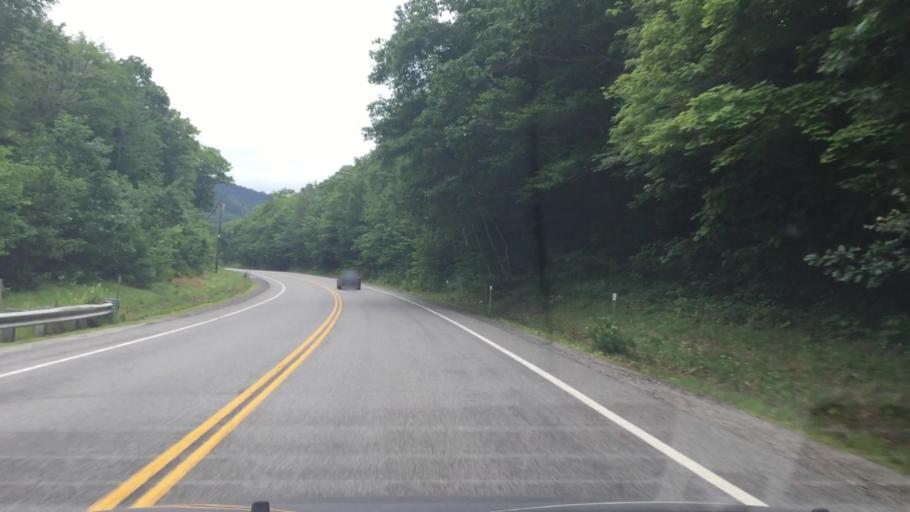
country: US
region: New Hampshire
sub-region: Carroll County
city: North Conway
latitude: 44.1267
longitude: -71.3593
